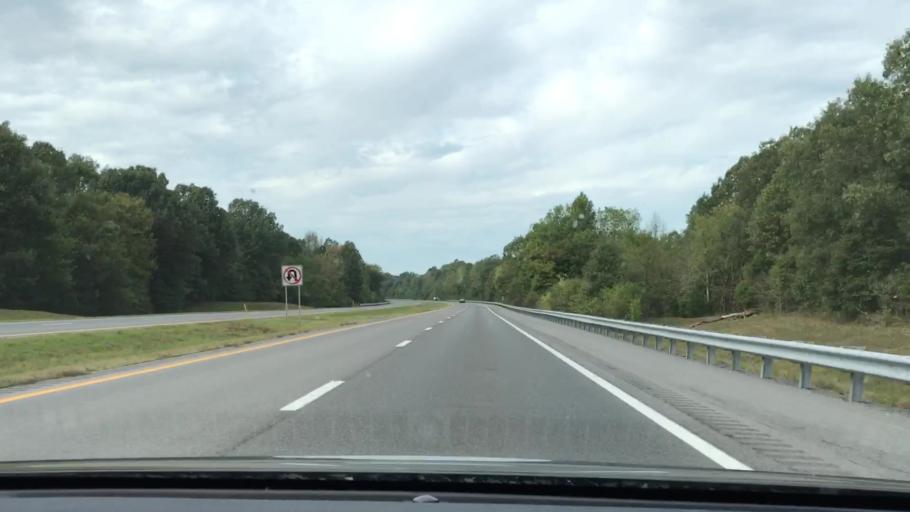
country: US
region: Kentucky
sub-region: Marshall County
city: Benton
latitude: 36.8218
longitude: -88.4759
